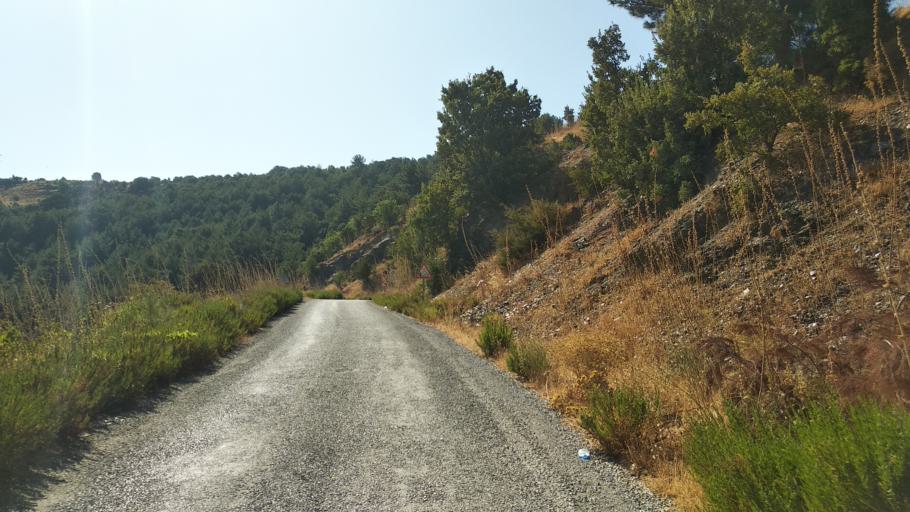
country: TR
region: Izmir
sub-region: Seferihisar
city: Seferhisar
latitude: 38.3297
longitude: 26.9465
